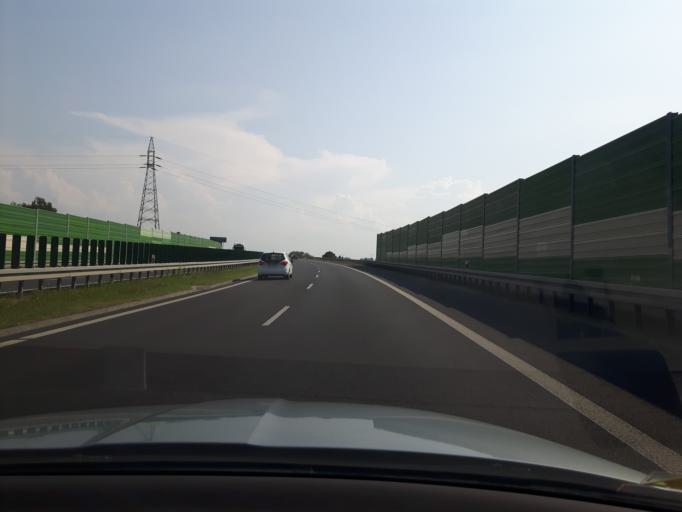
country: PL
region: Masovian Voivodeship
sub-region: Powiat plonski
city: Plonsk
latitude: 52.6173
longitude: 20.3877
